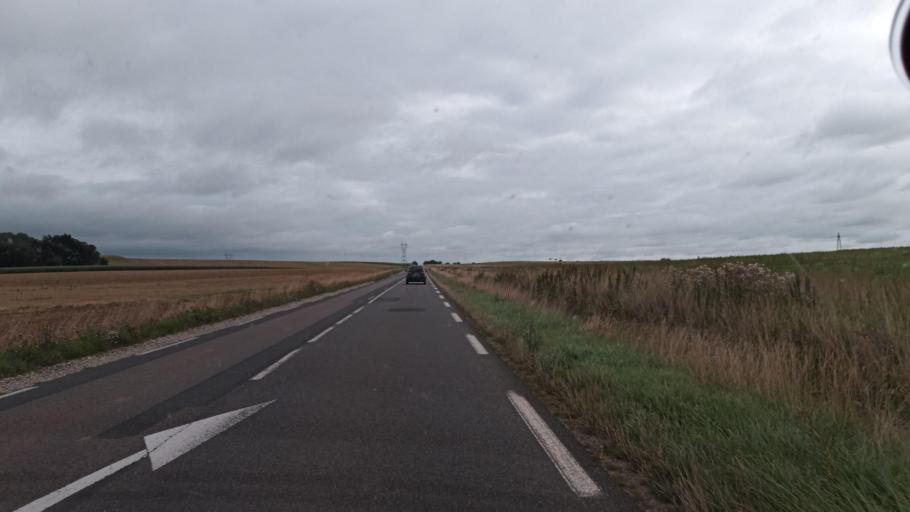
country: FR
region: Ile-de-France
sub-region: Departement de Seine-et-Marne
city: Voulx
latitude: 48.3230
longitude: 2.9528
